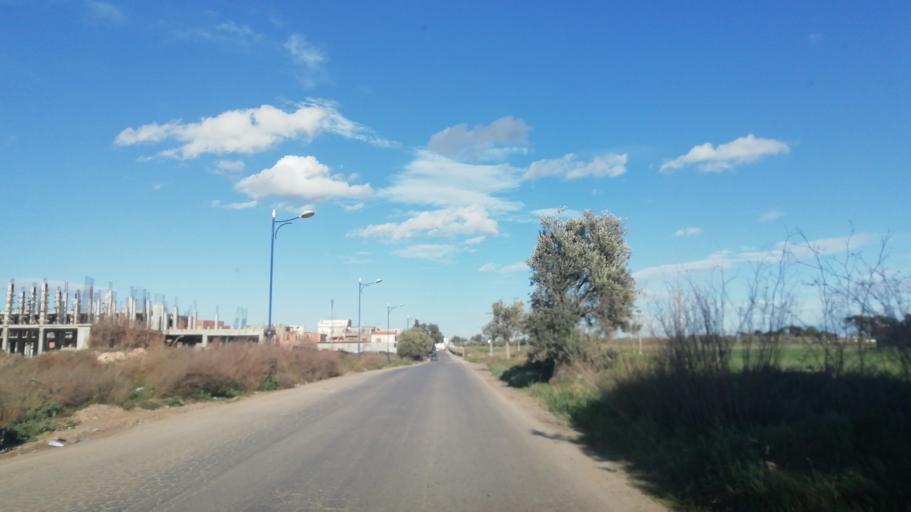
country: DZ
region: Oran
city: Sidi ech Chahmi
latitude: 35.6531
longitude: -0.5288
